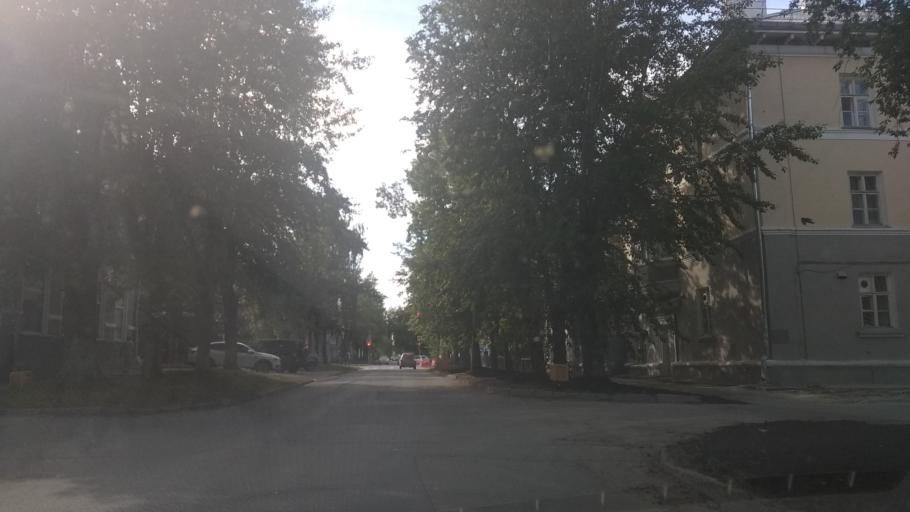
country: RU
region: Sverdlovsk
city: Yekaterinburg
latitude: 56.8993
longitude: 60.5901
